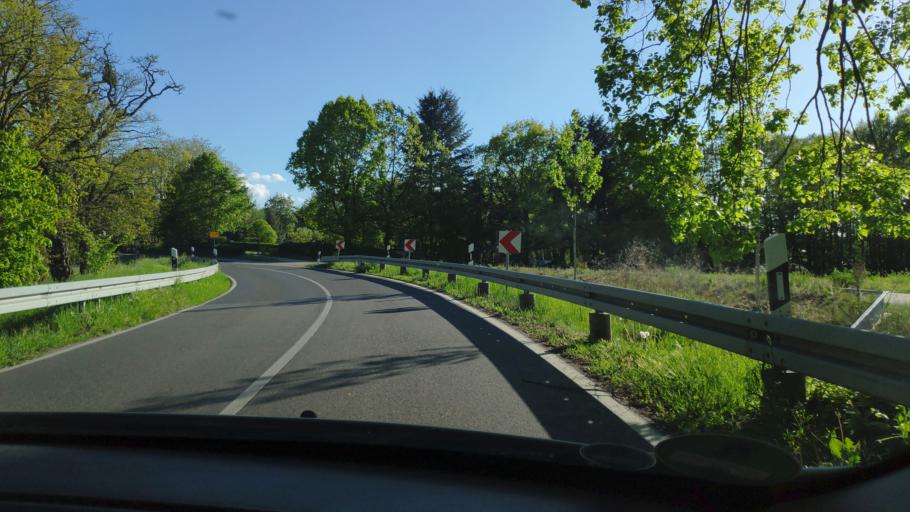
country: DE
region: Mecklenburg-Vorpommern
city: Wesenberg
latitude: 53.3246
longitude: 12.9717
